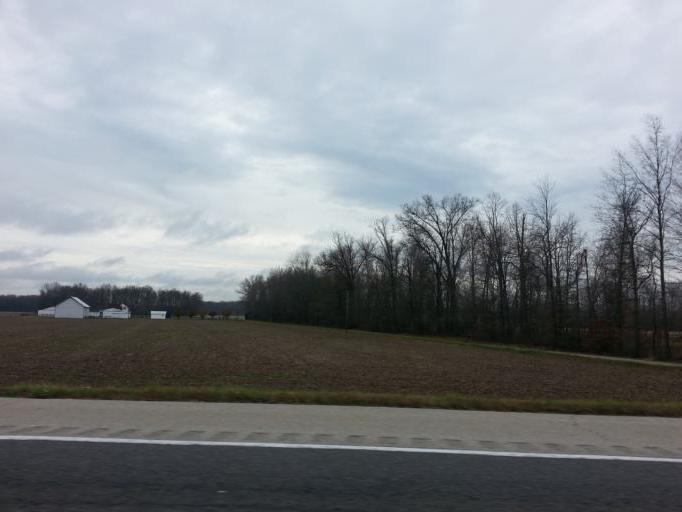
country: US
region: Indiana
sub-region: Ripley County
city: Batesville
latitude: 39.2858
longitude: -85.1602
